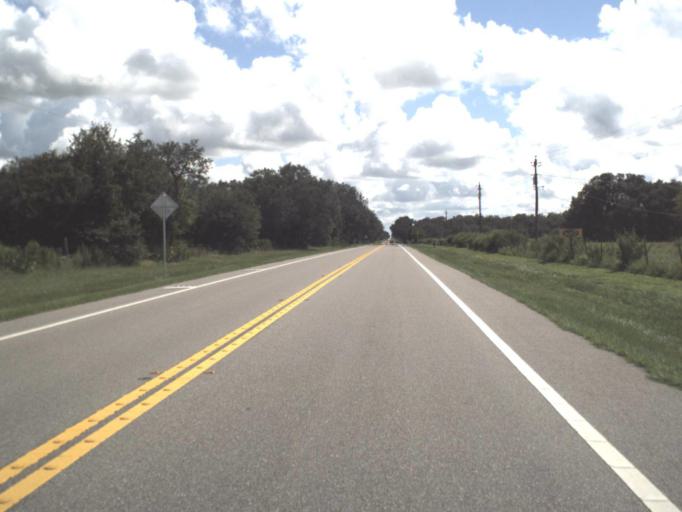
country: US
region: Florida
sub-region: Sarasota County
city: Lake Sarasota
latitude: 27.3834
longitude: -82.2417
